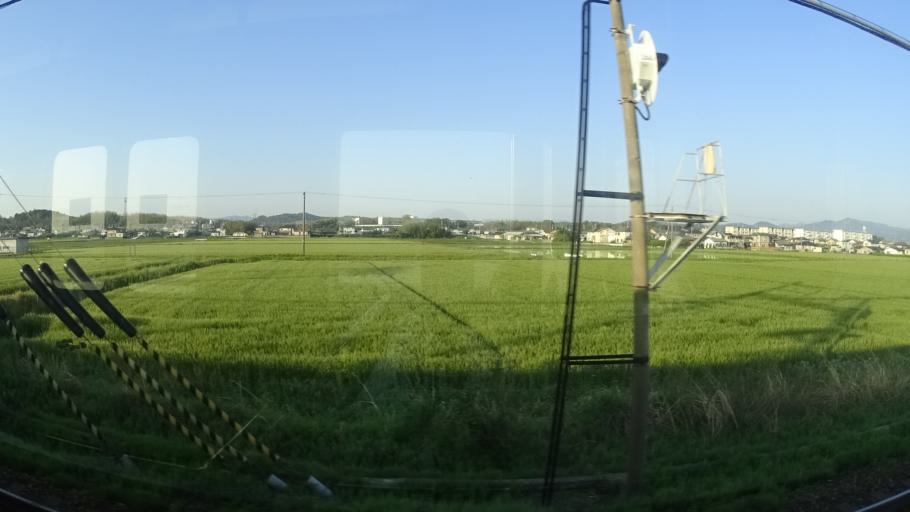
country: JP
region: Mie
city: Ise
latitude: 34.5533
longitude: 136.5727
